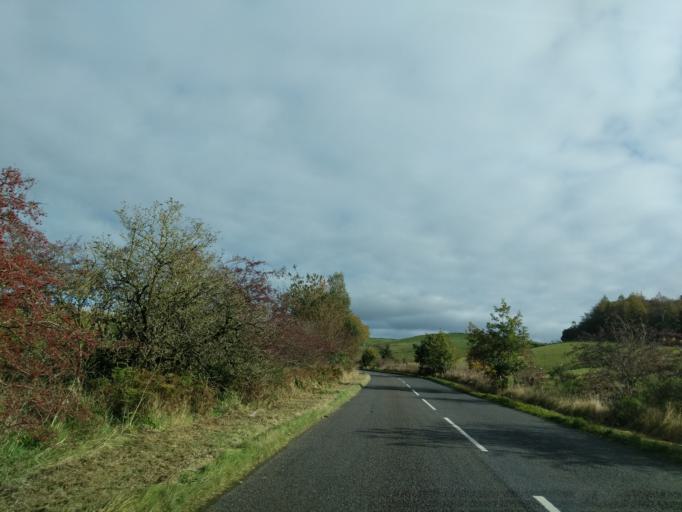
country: GB
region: Scotland
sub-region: Dumfries and Galloway
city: Castle Douglas
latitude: 55.0804
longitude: -4.1245
